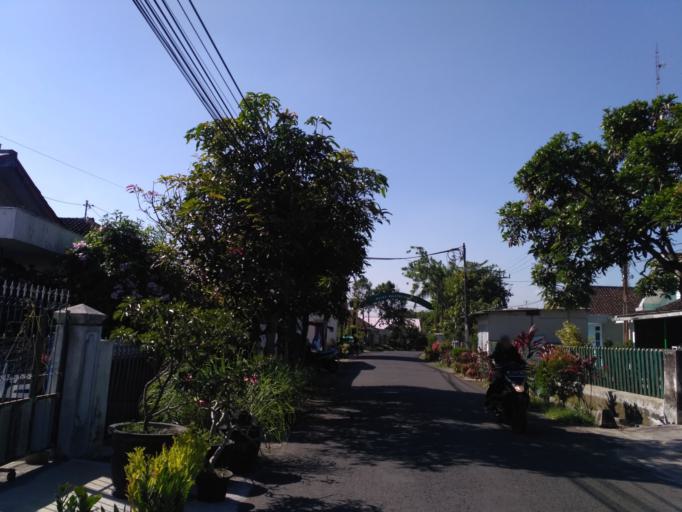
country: ID
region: East Java
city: Singosari
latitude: -7.9308
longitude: 112.6565
